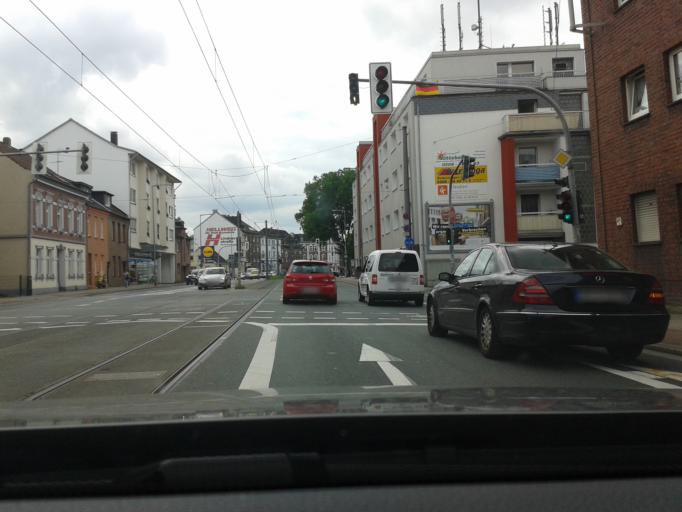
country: DE
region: North Rhine-Westphalia
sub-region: Regierungsbezirk Dusseldorf
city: Oberhausen
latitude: 51.4667
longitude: 6.8641
